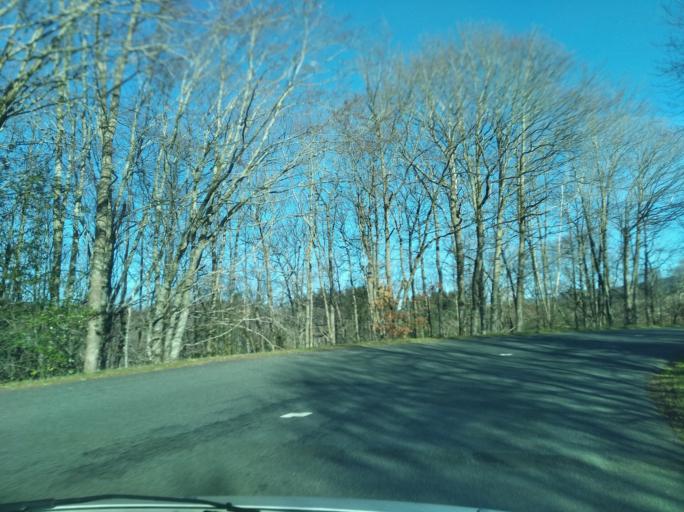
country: FR
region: Auvergne
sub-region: Departement de l'Allier
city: Le Mayet-de-Montagne
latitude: 46.1056
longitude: 3.7604
